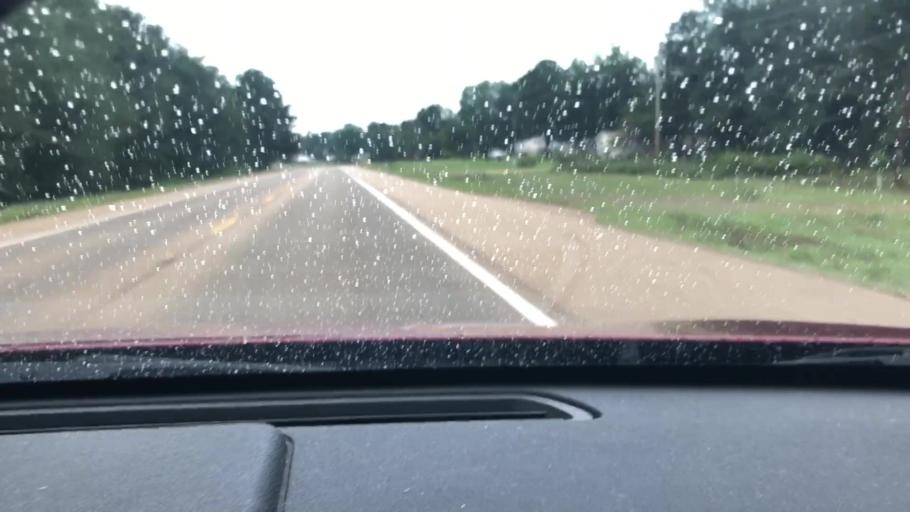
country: US
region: Arkansas
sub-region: Lafayette County
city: Stamps
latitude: 33.3590
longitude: -93.4255
